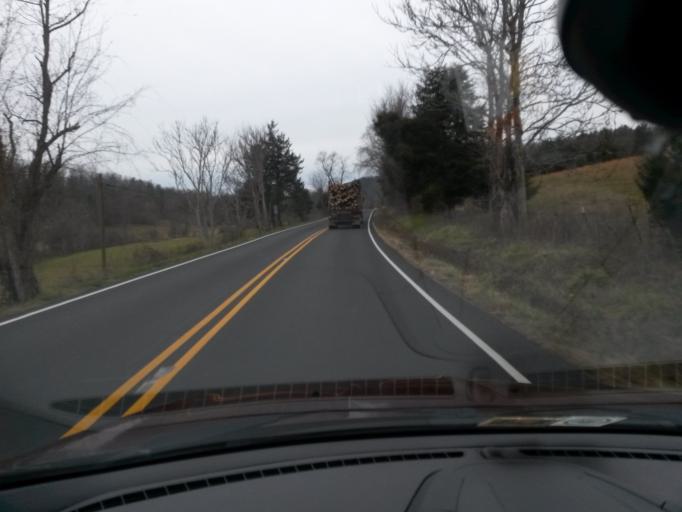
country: US
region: Virginia
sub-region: Amherst County
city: Amherst
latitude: 37.6601
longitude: -79.1546
